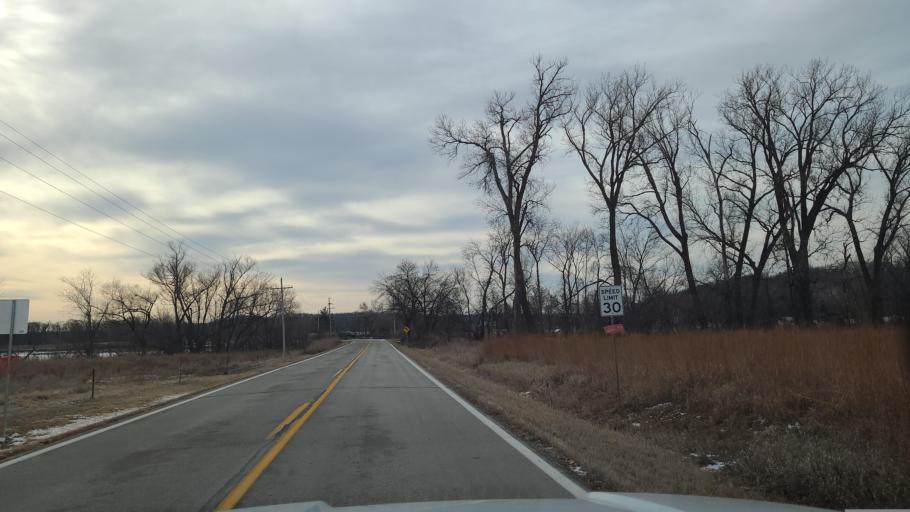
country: US
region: Kansas
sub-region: Douglas County
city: Lawrence
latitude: 39.0145
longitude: -95.2935
